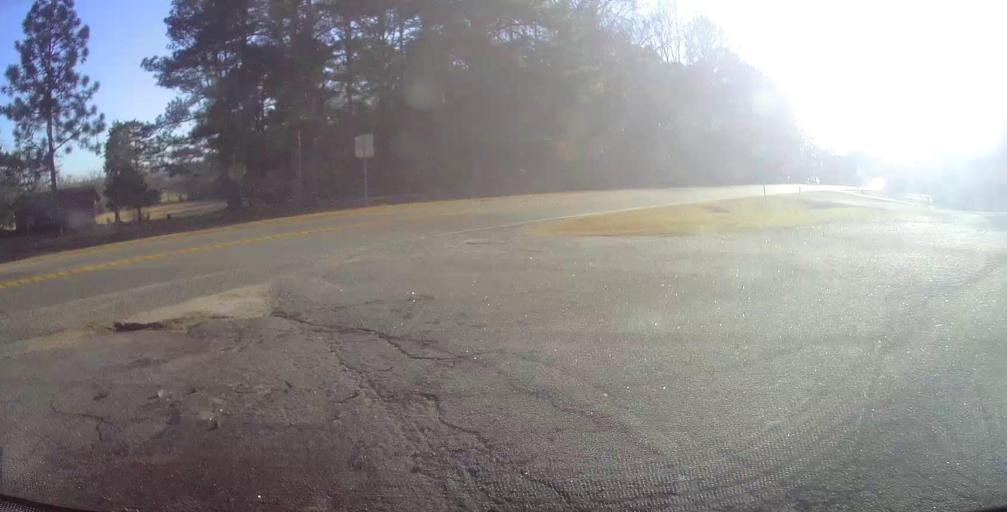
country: US
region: Georgia
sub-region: Meriwether County
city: Manchester
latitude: 32.8415
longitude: -84.6245
